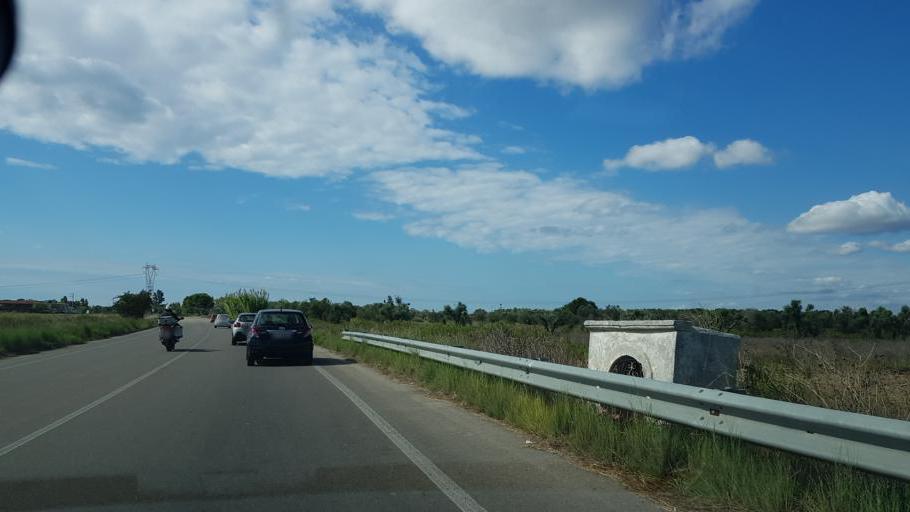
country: IT
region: Apulia
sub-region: Provincia di Lecce
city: Leverano
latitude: 40.3110
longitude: 18.0225
